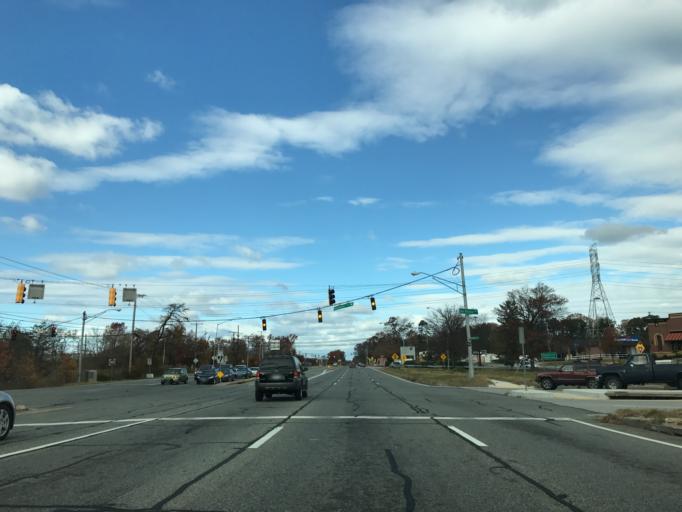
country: US
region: Maryland
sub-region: Anne Arundel County
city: South Gate
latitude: 39.1359
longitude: -76.5984
